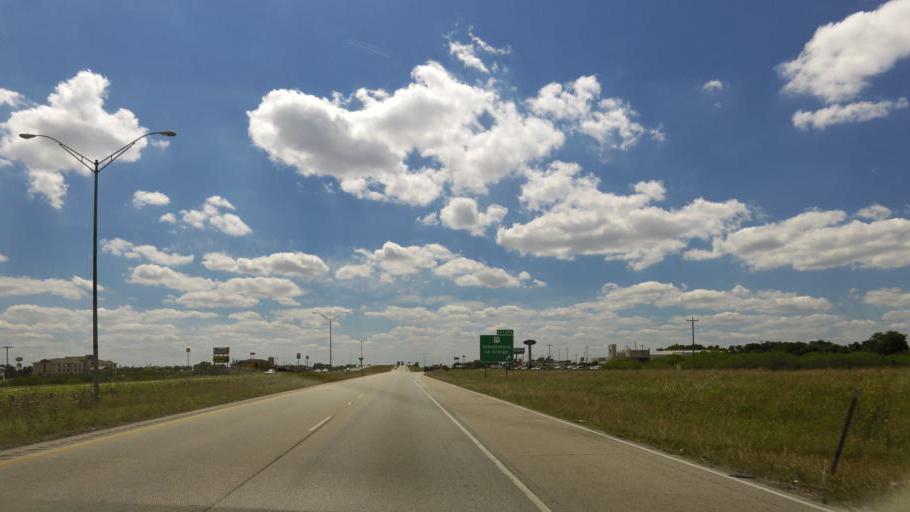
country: US
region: Texas
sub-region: Fayette County
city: Schulenburg
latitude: 29.6946
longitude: -96.8960
